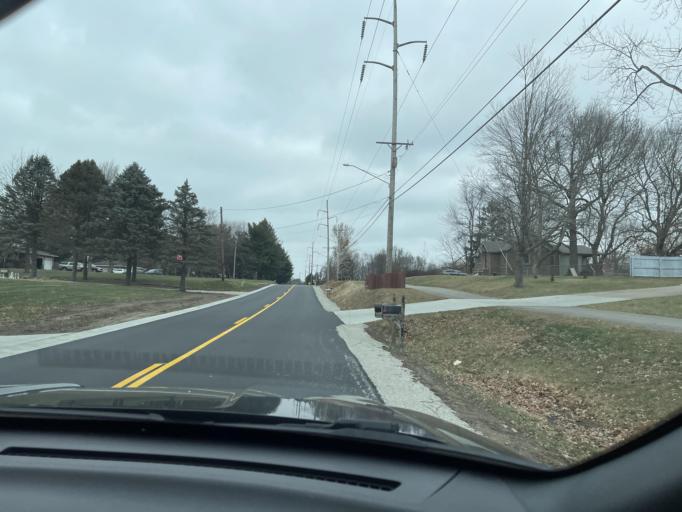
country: US
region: Illinois
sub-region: Sangamon County
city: Rochester
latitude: 39.7699
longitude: -89.5788
